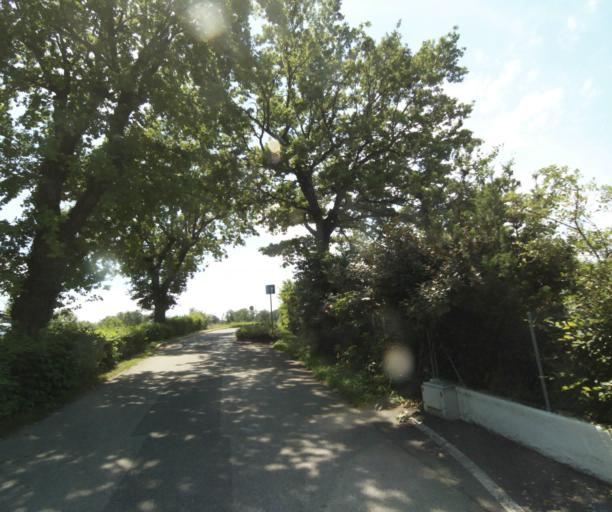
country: FR
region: Rhone-Alpes
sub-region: Departement de la Haute-Savoie
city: Messery
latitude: 46.3608
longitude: 6.3057
